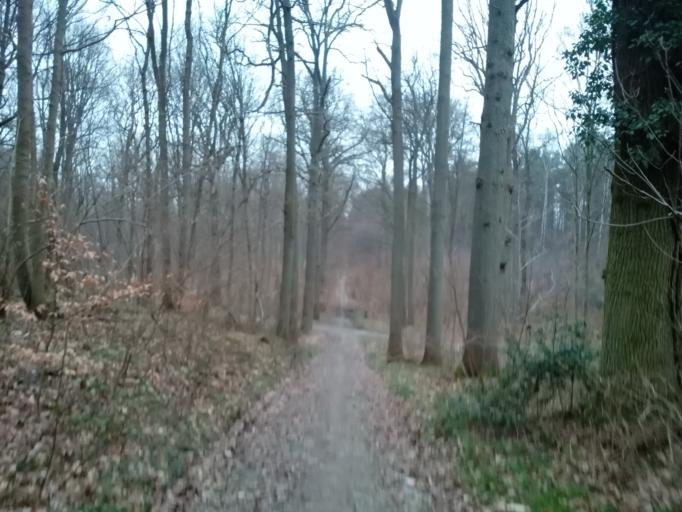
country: BE
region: Flanders
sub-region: Provincie Vlaams-Brabant
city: Bierbeek
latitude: 50.8003
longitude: 4.7202
